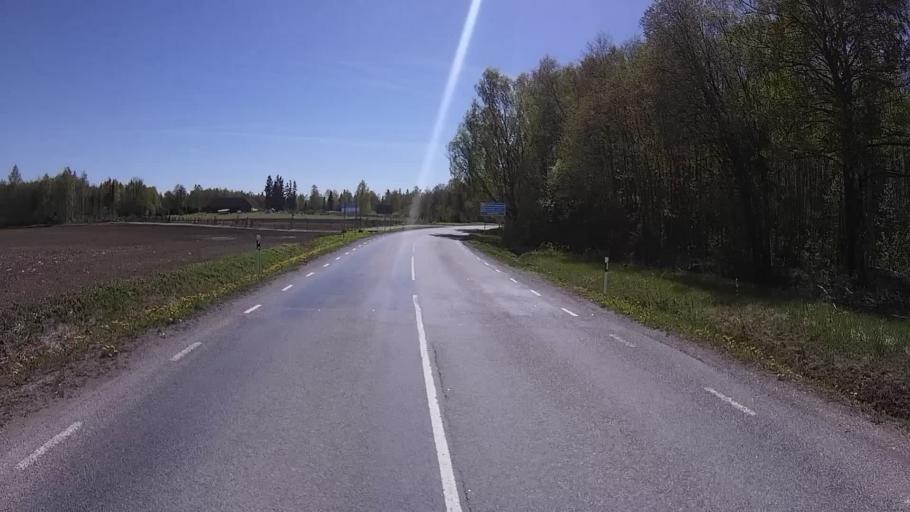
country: EE
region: Harju
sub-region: Raasiku vald
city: Raasiku
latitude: 59.0867
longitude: 25.1770
